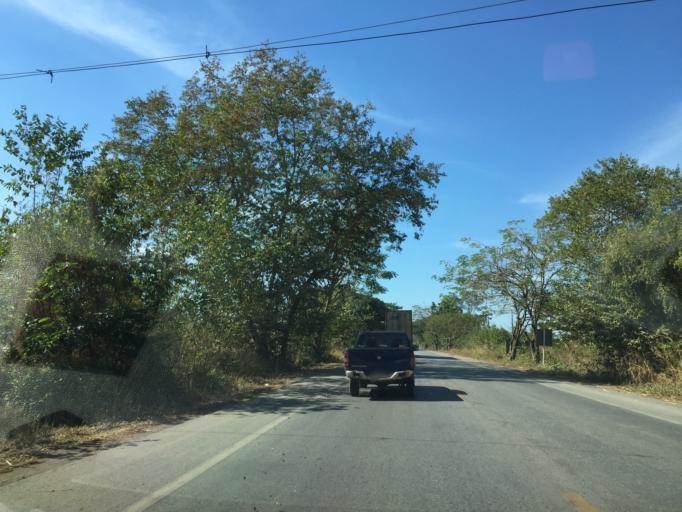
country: TH
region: Changwat Nong Bua Lamphu
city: Na Klang
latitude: 17.3118
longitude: 102.1725
